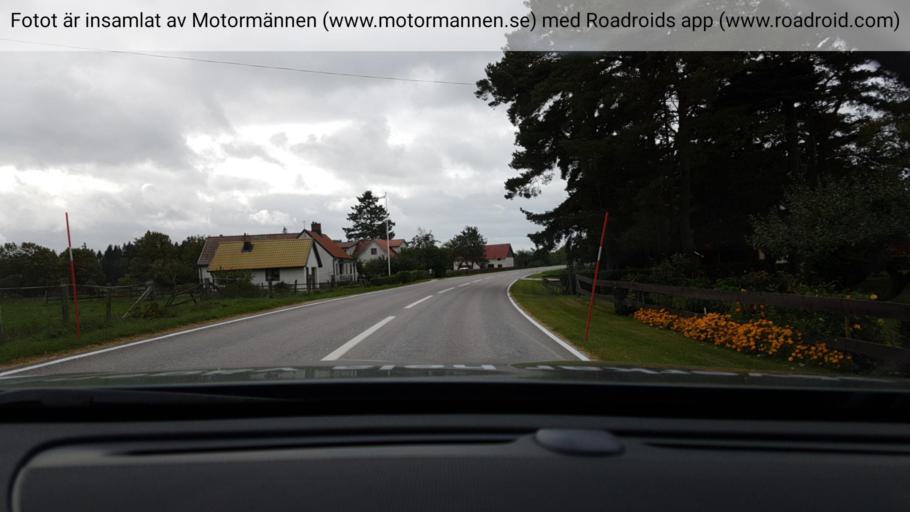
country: SE
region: Gotland
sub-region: Gotland
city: Klintehamn
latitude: 57.3256
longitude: 18.1927
